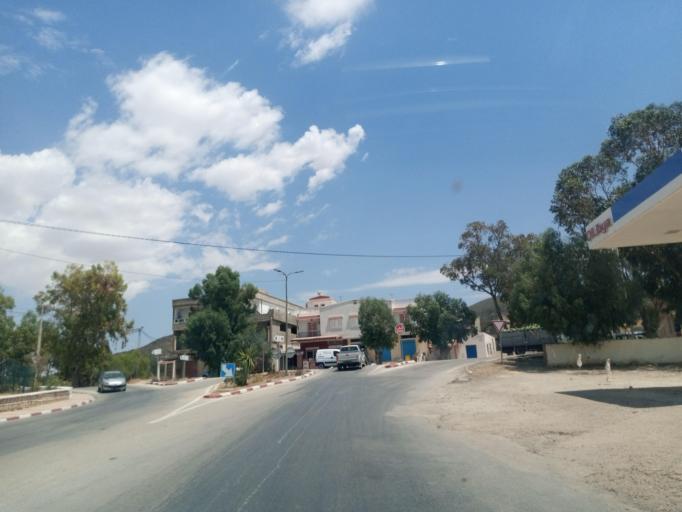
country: TN
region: Kef
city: Nibbar
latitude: 36.3079
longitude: 8.7741
